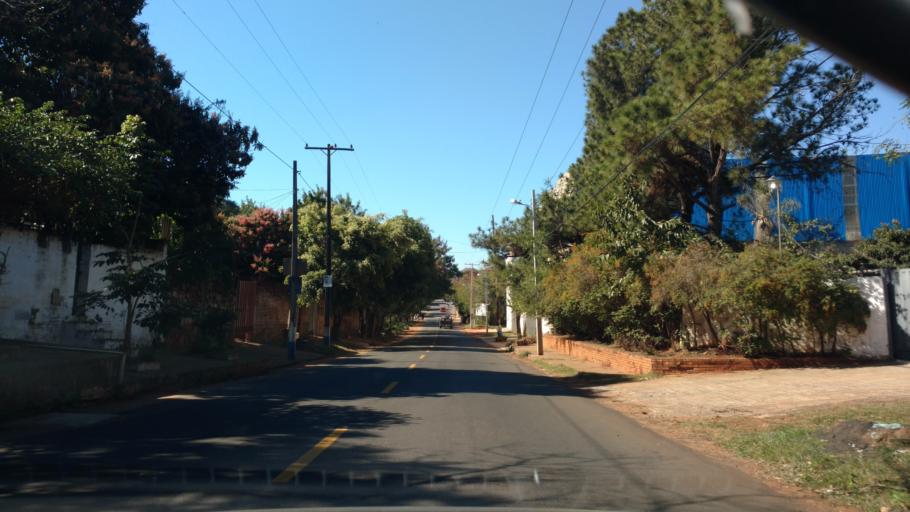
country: PY
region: Central
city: Itaugua
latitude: -25.3898
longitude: -57.3610
